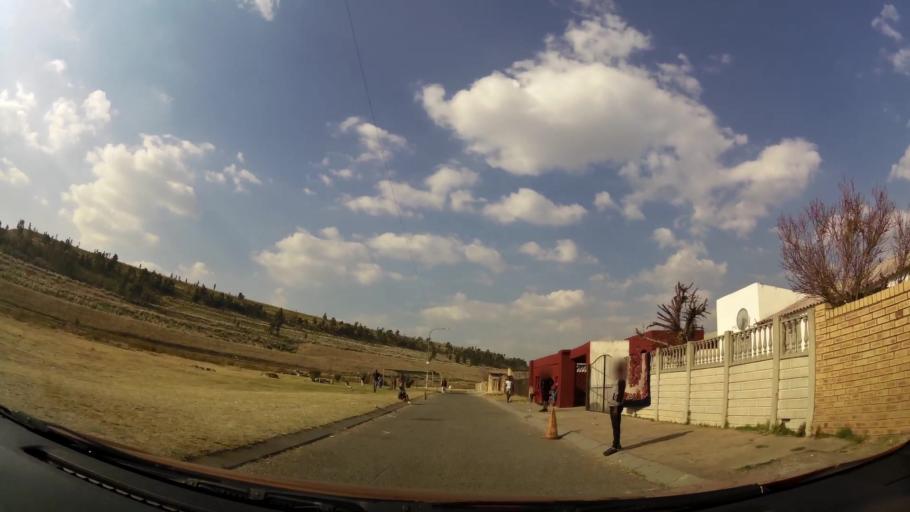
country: ZA
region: Gauteng
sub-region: City of Johannesburg Metropolitan Municipality
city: Soweto
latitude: -26.2323
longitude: 27.9466
